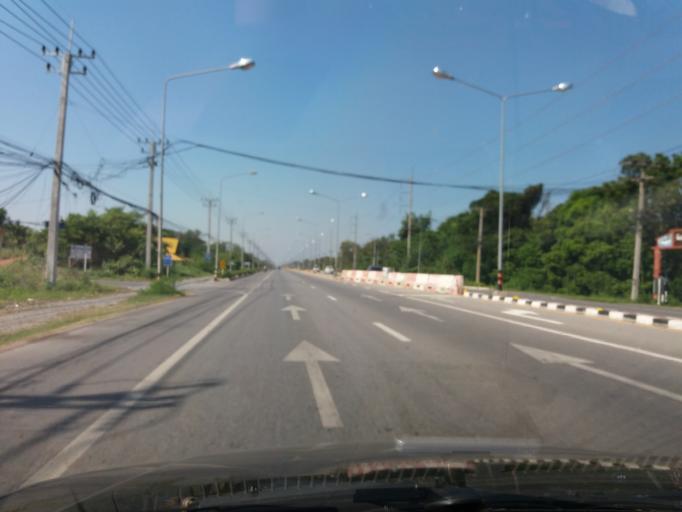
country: TH
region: Chai Nat
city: Chai Nat
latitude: 15.1998
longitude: 100.1240
